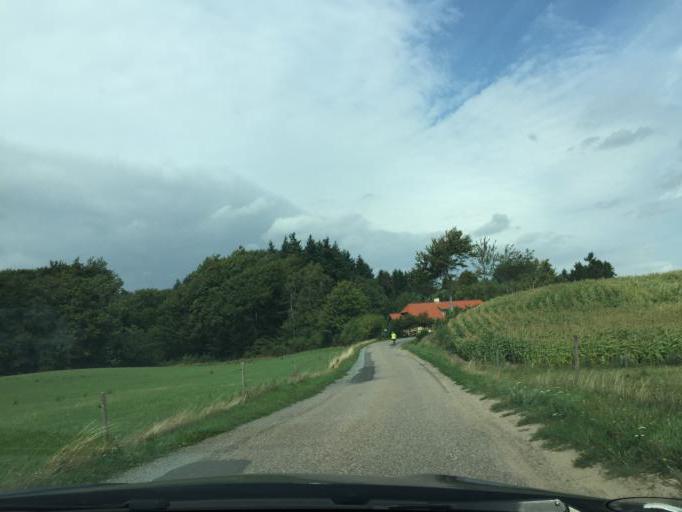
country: DK
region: South Denmark
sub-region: Assens Kommune
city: Vissenbjerg
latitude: 55.4106
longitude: 10.1907
